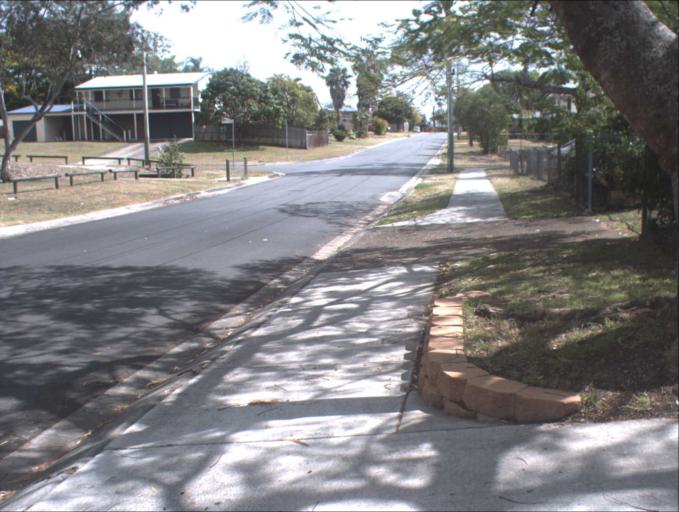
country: AU
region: Queensland
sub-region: Logan
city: Beenleigh
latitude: -27.7176
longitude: 153.1910
